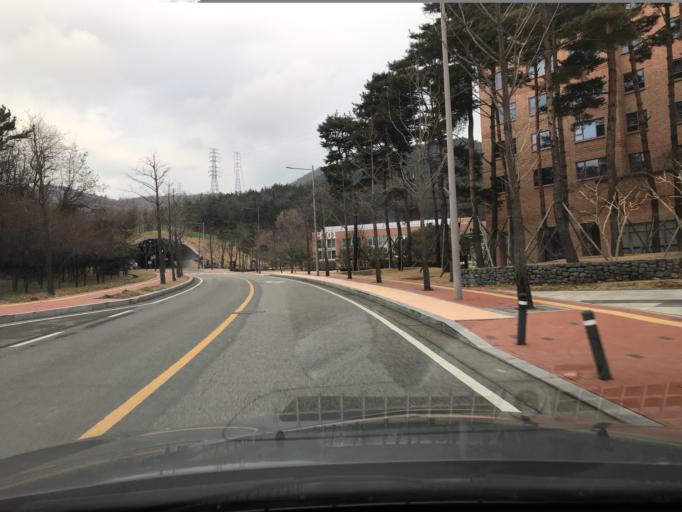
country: KR
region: Daegu
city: Hwawon
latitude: 35.7033
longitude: 128.4613
